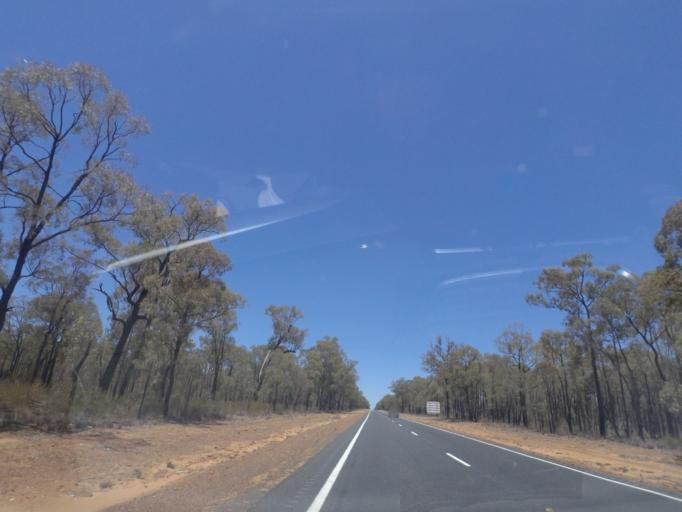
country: AU
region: New South Wales
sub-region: Narrabri
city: Narrabri
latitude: -30.7265
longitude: 149.5228
